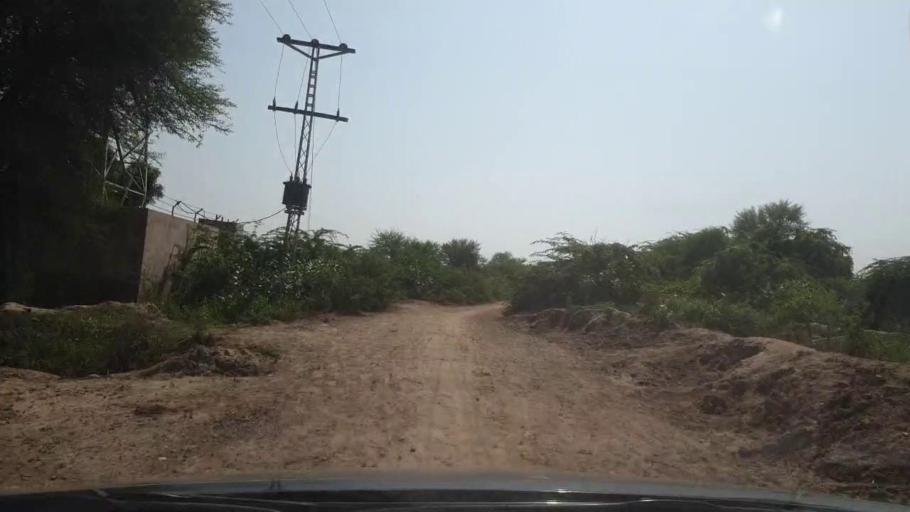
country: PK
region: Sindh
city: Naukot
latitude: 24.8102
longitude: 69.2616
